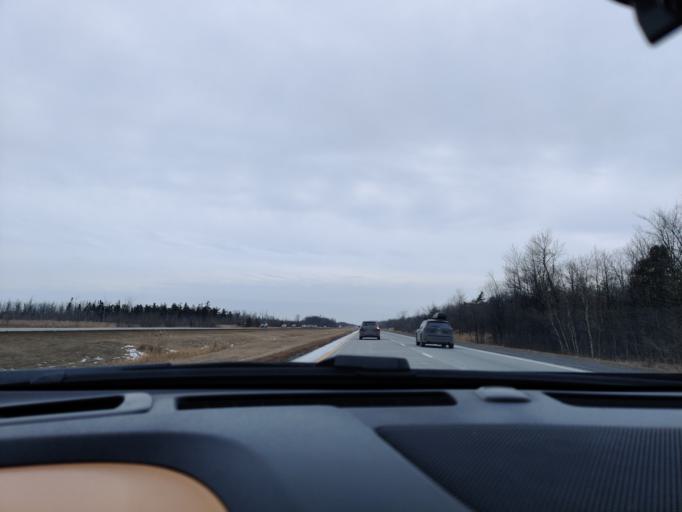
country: US
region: New York
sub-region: St. Lawrence County
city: Massena
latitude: 45.0030
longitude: -75.0186
